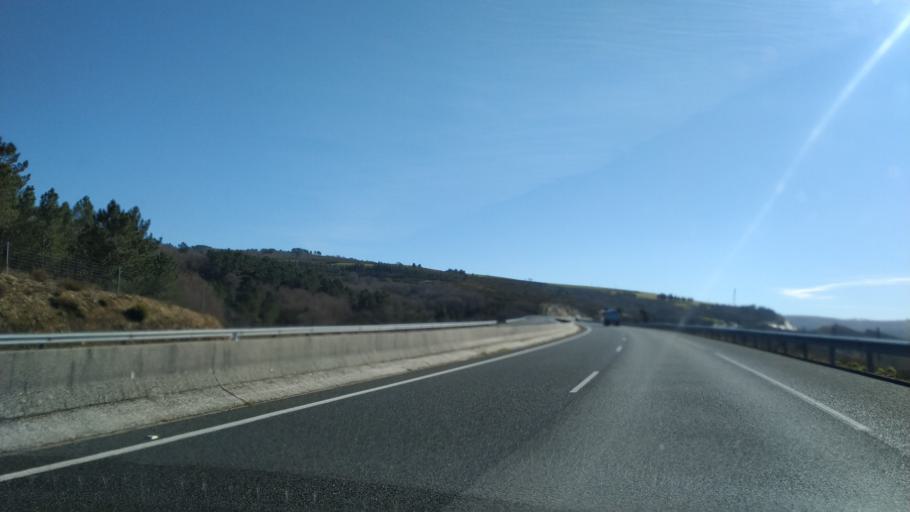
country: ES
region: Galicia
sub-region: Provincia de Pontevedra
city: Lalin
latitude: 42.6022
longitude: -8.0967
